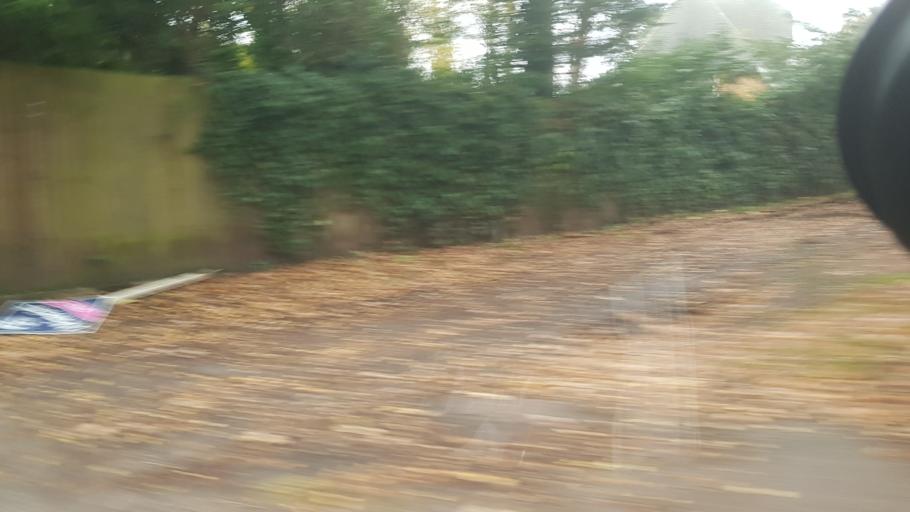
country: GB
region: England
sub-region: Hampshire
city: Farnborough
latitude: 51.3131
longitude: -0.7762
